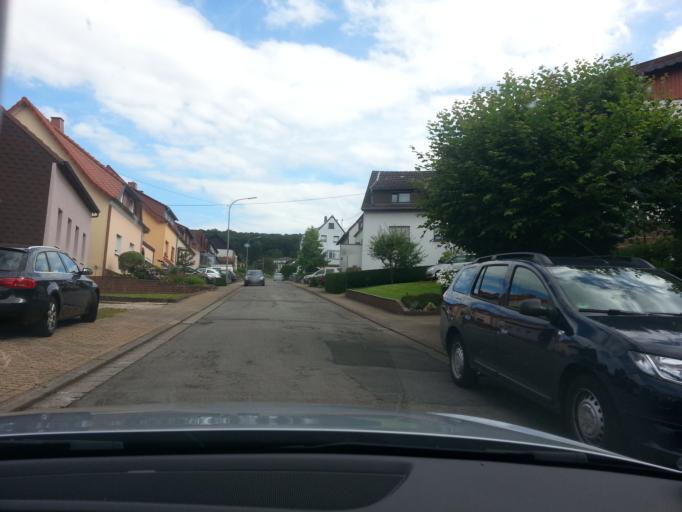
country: DE
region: Saarland
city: Marpingen
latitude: 49.4483
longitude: 7.0591
